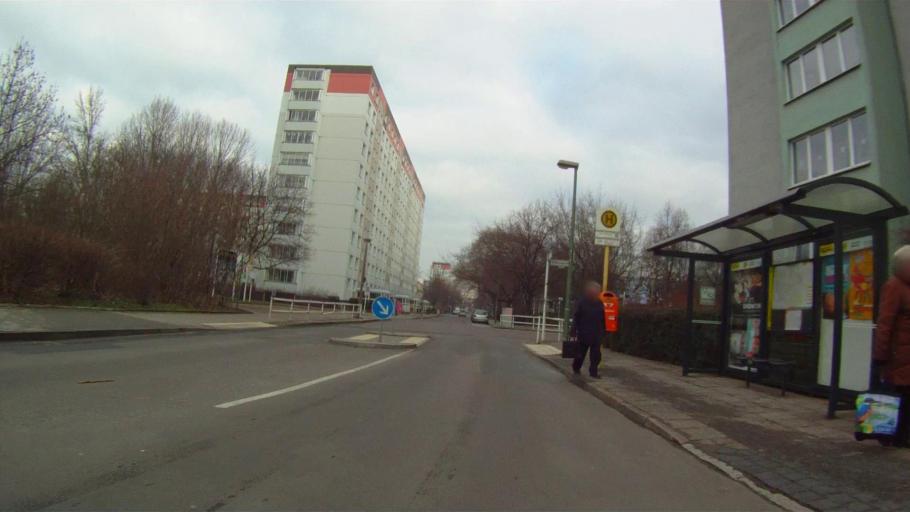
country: DE
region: Berlin
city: Friedrichsfelde
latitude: 52.4934
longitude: 13.5082
